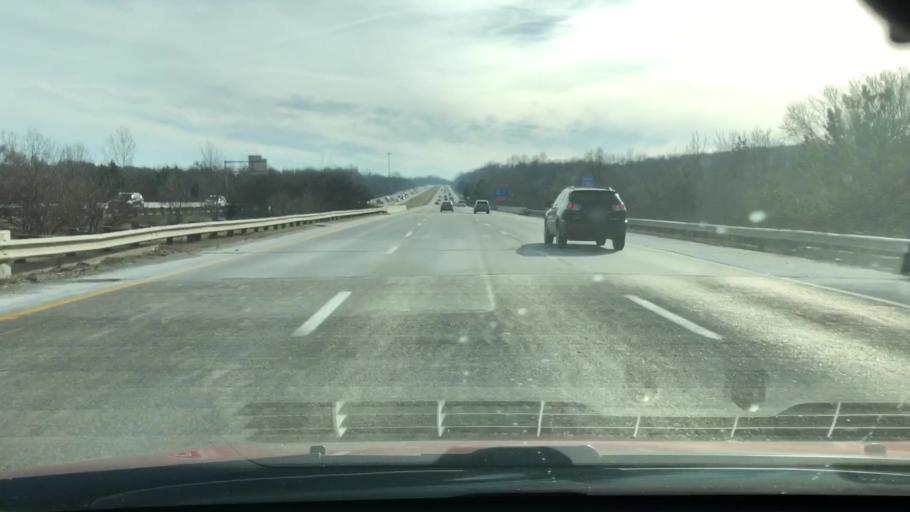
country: US
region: Ohio
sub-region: Greene County
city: Beavercreek
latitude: 39.7258
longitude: -84.0909
